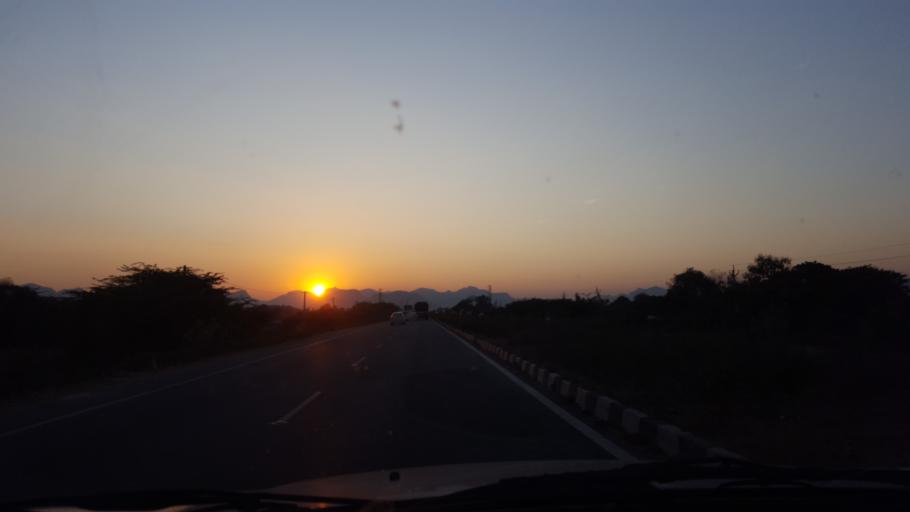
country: IN
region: Andhra Pradesh
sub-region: Chittoor
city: Tirupati
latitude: 13.6034
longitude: 79.3798
